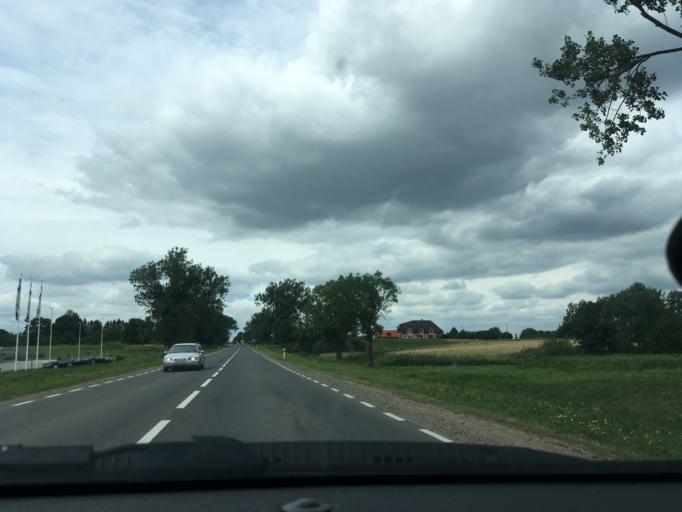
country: PL
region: Podlasie
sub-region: Powiat augustowski
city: Augustow
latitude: 53.8423
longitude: 22.9598
